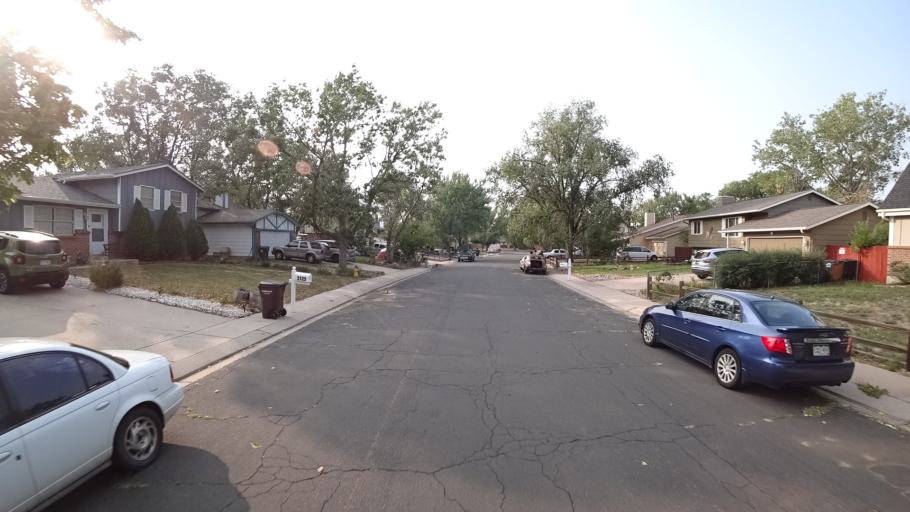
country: US
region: Colorado
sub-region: El Paso County
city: Stratmoor
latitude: 38.8020
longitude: -104.7449
